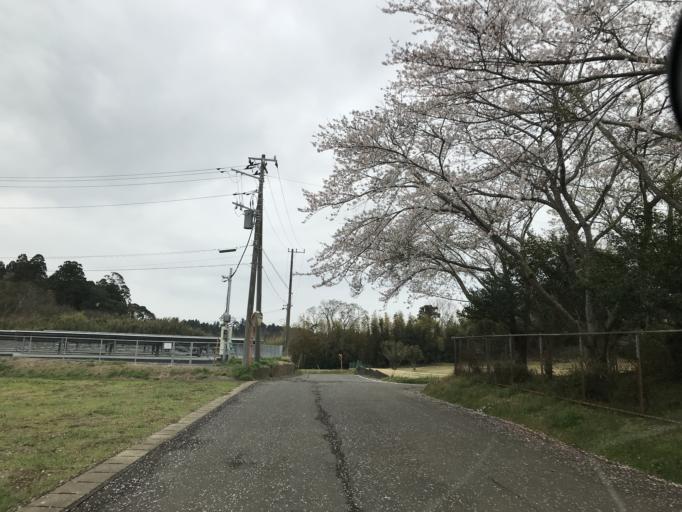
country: JP
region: Chiba
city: Sawara
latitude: 35.8105
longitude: 140.5069
